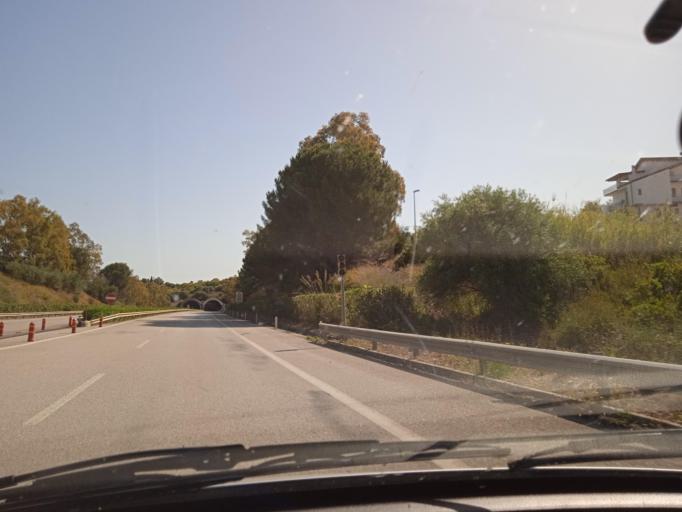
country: IT
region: Sicily
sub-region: Messina
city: Sant'Agata di Militello
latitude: 38.0730
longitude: 14.6574
